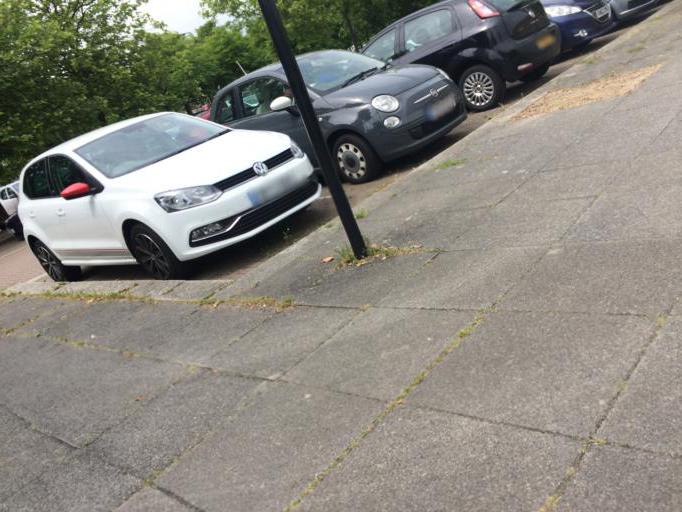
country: GB
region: England
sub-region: Milton Keynes
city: Milton Keynes
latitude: 52.0381
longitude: -0.7554
